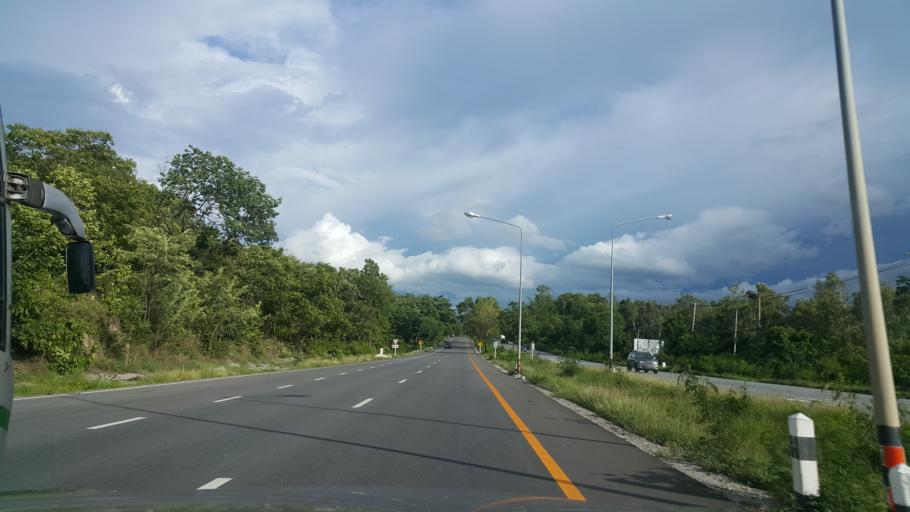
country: TH
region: Tak
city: Ban Tak
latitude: 16.9771
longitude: 99.1272
